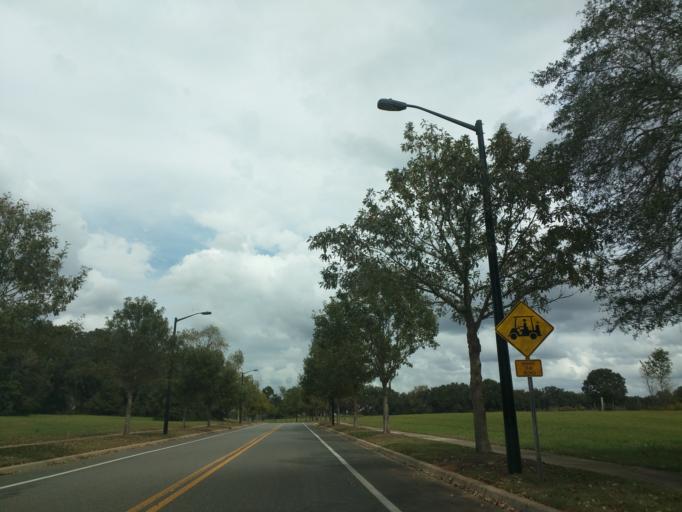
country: US
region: Florida
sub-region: Leon County
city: Woodville
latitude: 30.3879
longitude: -84.2093
